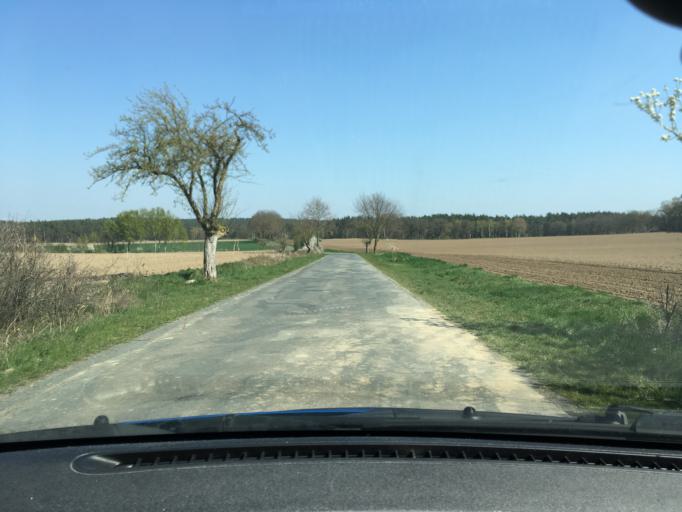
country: DE
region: Lower Saxony
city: Reinstorf
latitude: 53.2000
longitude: 10.5951
